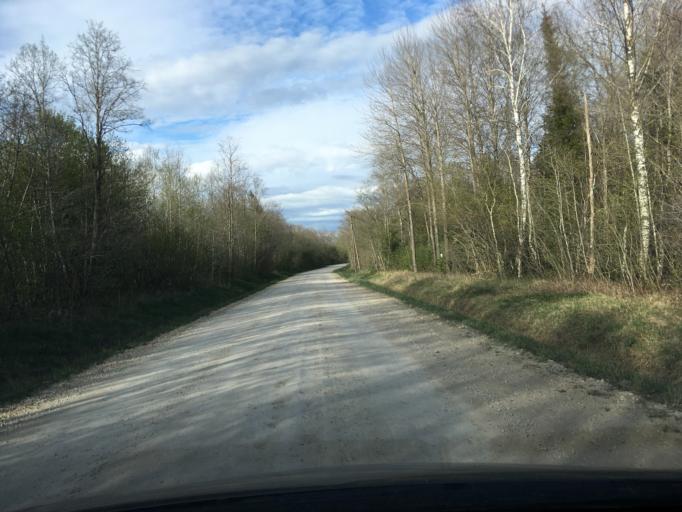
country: EE
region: Raplamaa
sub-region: Maerjamaa vald
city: Marjamaa
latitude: 59.0001
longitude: 24.3747
